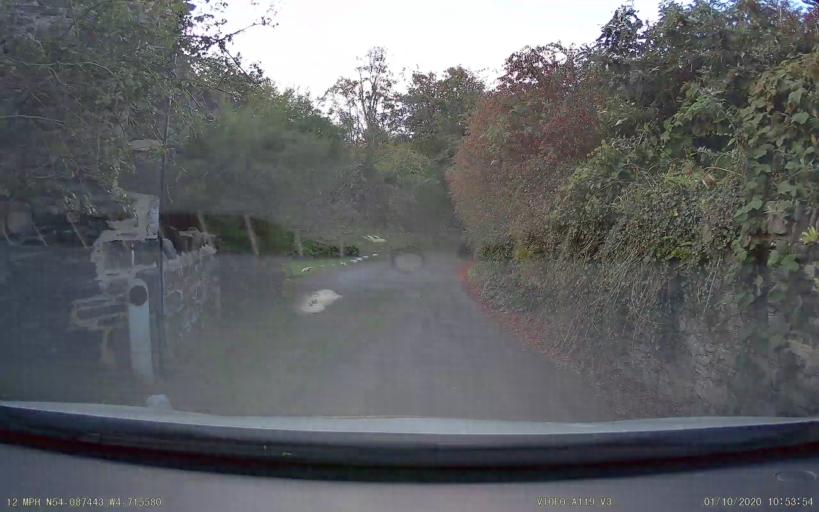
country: IM
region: Port Erin
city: Port Erin
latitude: 54.0874
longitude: -4.7156
